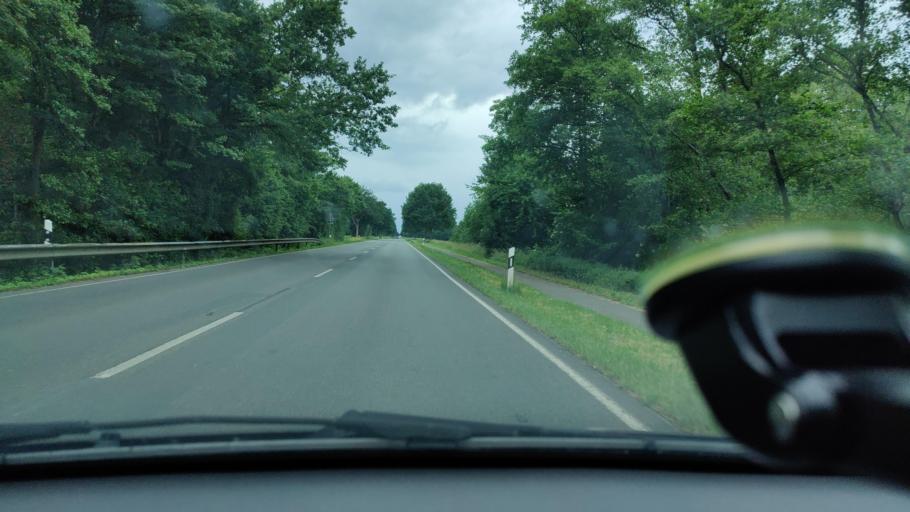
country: DE
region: North Rhine-Westphalia
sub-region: Regierungsbezirk Dusseldorf
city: Weeze
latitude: 51.6659
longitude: 6.2258
